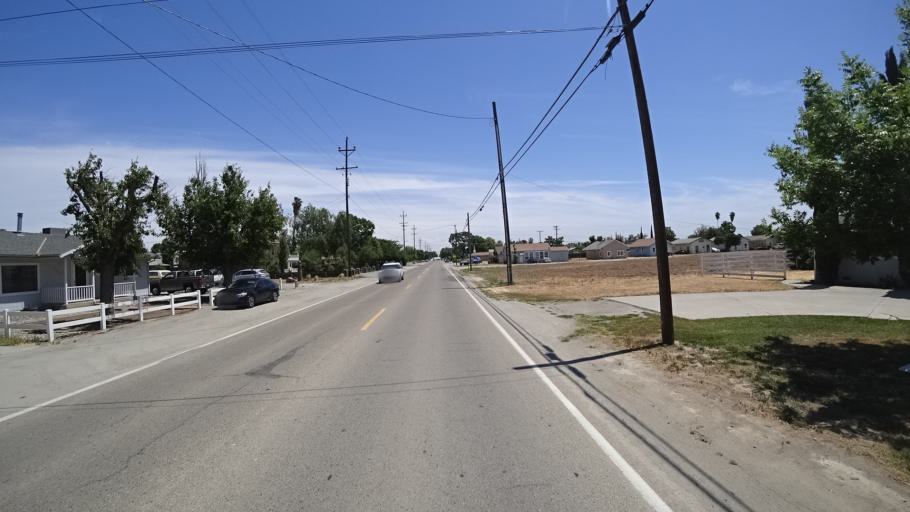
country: US
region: California
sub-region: Kings County
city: Armona
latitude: 36.3136
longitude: -119.7150
